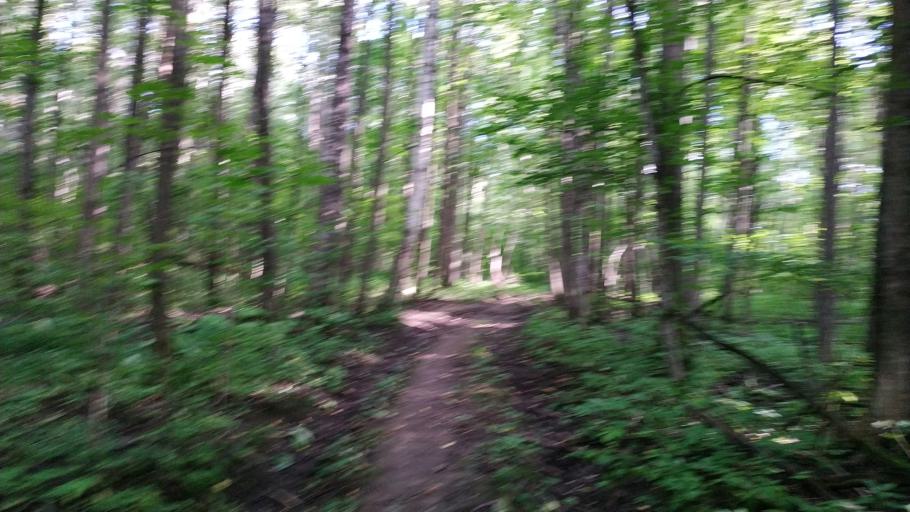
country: RU
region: Chuvashia
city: Novyye Lapsary
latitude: 56.1229
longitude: 47.1239
